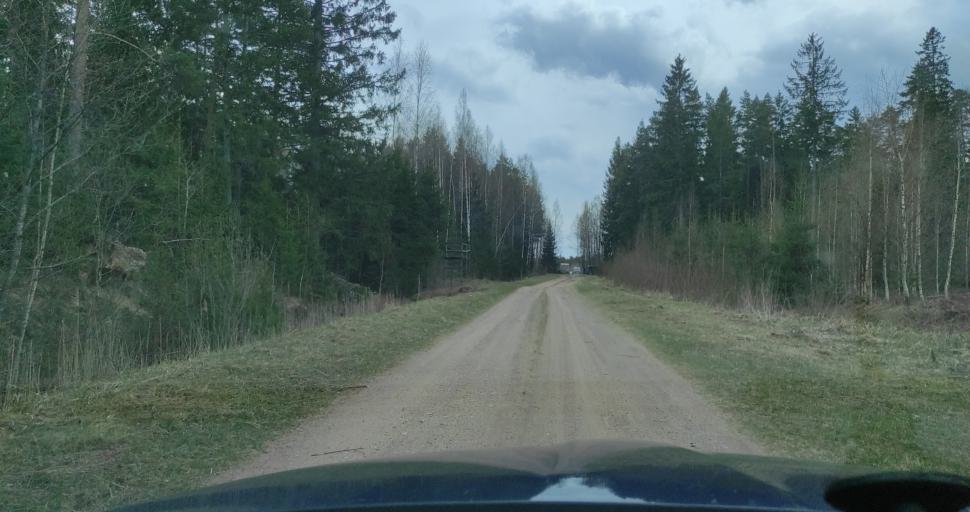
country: LV
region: Dundaga
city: Dundaga
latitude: 57.3584
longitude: 22.1526
